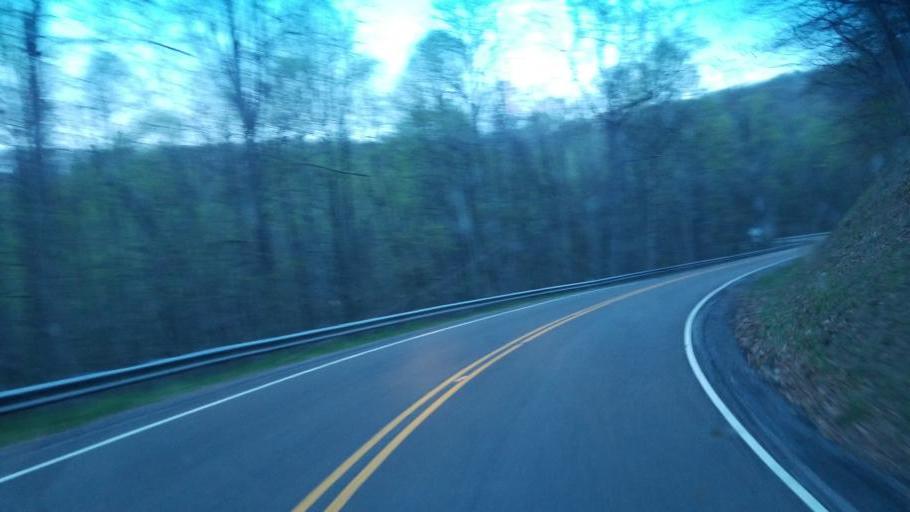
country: US
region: Virginia
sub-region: Smyth County
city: Atkins
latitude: 36.8128
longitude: -81.4251
